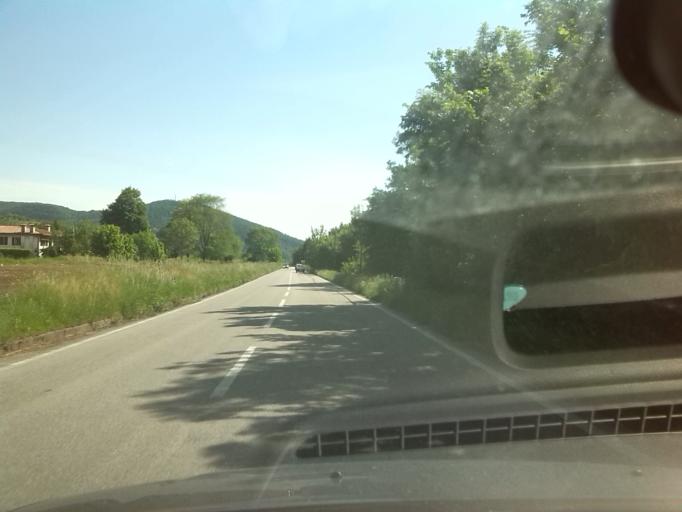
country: IT
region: Friuli Venezia Giulia
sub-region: Provincia di Udine
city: San Pietro al Natisone
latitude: 46.1359
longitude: 13.4853
